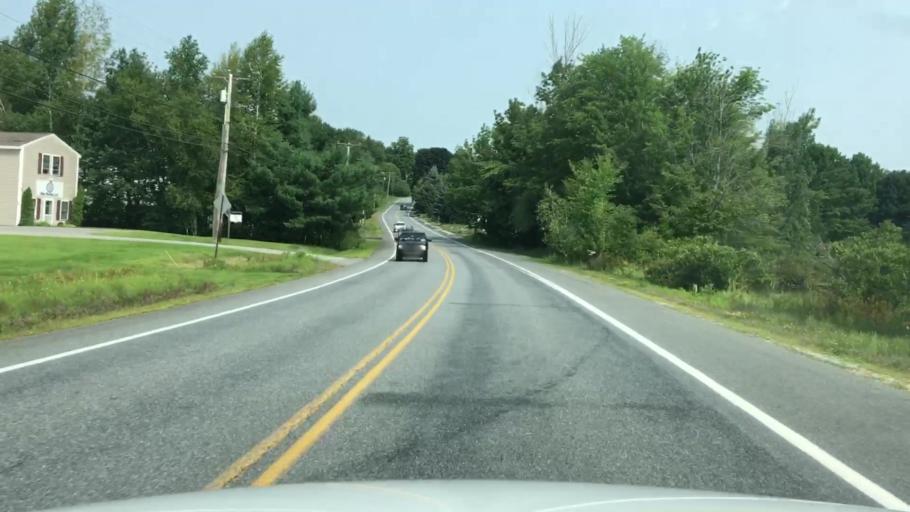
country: US
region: Maine
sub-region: Kennebec County
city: Winthrop
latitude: 44.3102
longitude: -69.9767
